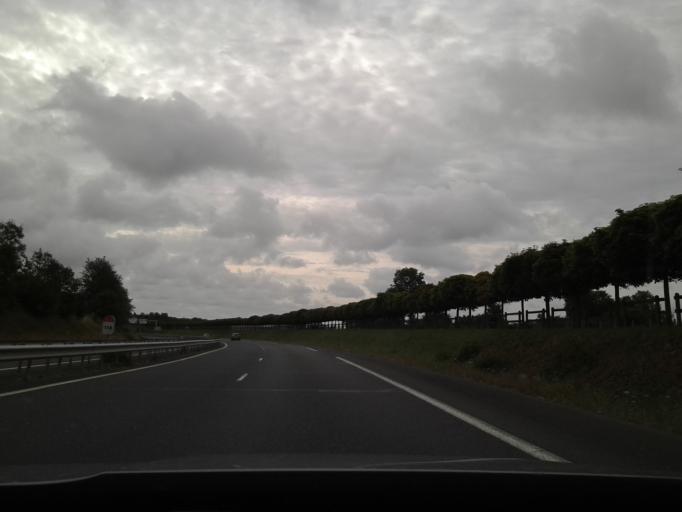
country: FR
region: Lower Normandy
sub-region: Departement du Calvados
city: Grandcamp-Maisy
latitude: 49.3404
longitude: -1.0155
